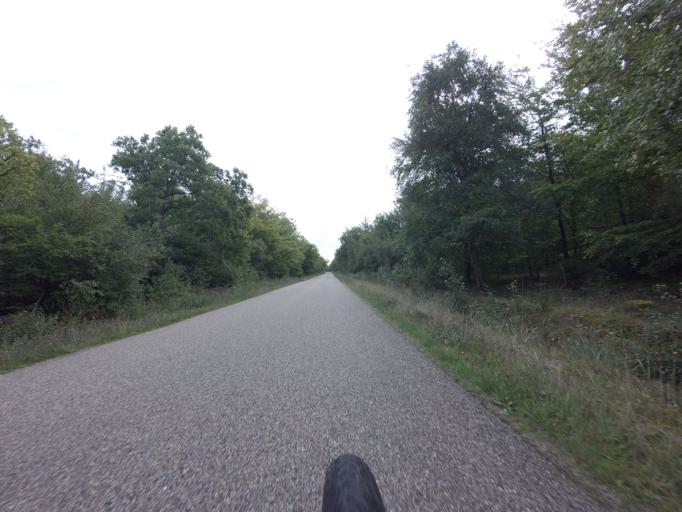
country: DK
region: North Denmark
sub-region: Hjorring Kommune
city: Hirtshals
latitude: 57.5797
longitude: 10.0340
